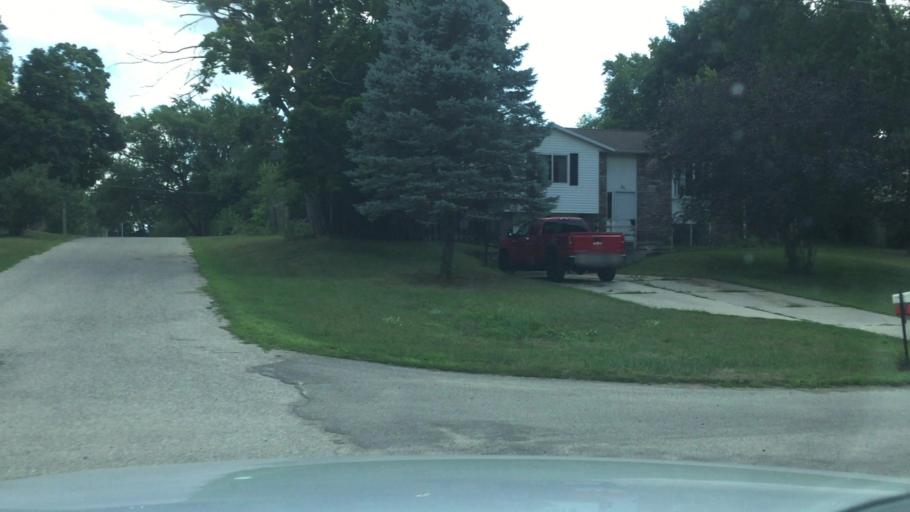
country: US
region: Michigan
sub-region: Ionia County
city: Belding
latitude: 43.1025
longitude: -85.2365
